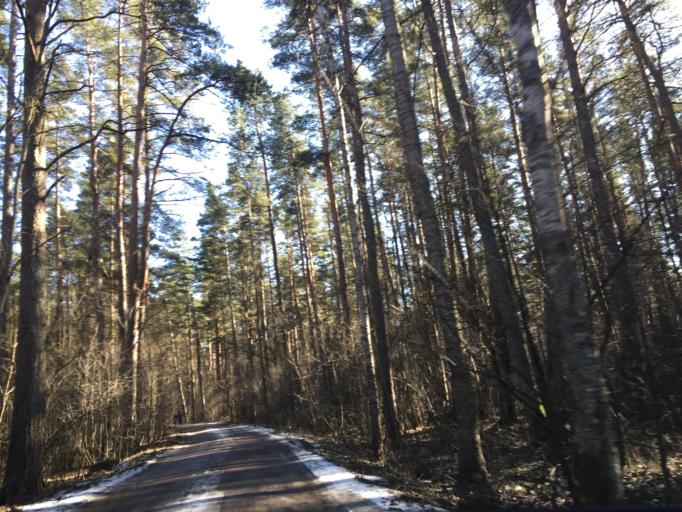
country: LV
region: Babite
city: Pinki
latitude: 56.9686
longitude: 23.9863
